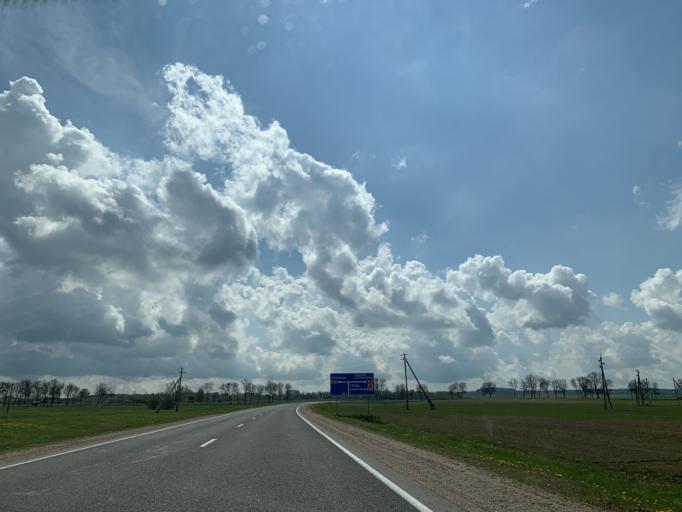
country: BY
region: Minsk
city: Nyasvizh
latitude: 53.2322
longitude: 26.7215
